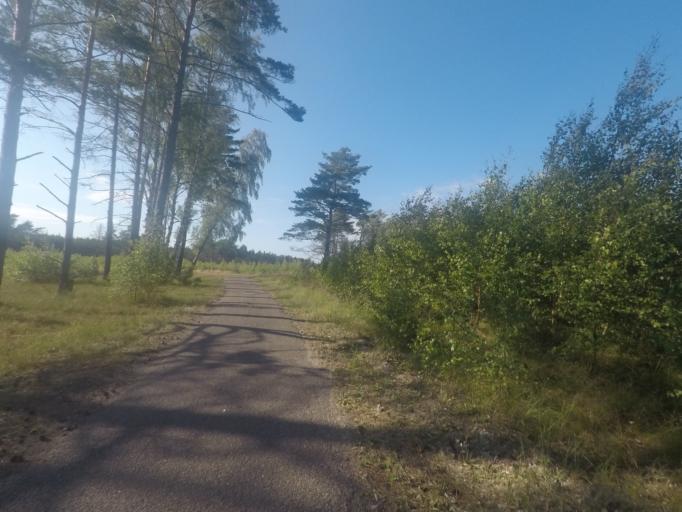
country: LT
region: Klaipedos apskritis
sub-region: Klaipeda
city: Klaipeda
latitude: 55.5876
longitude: 21.1128
